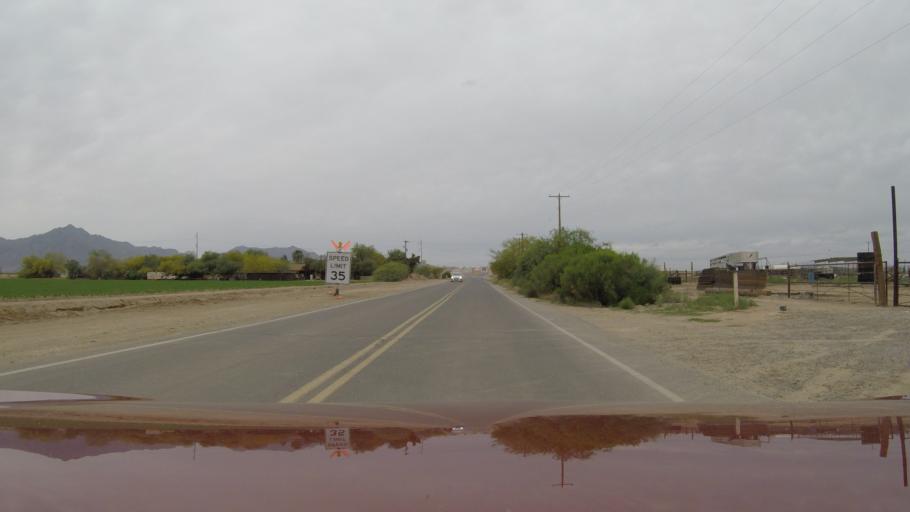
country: US
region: Arizona
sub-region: Maricopa County
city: Laveen
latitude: 33.3484
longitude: -112.1848
